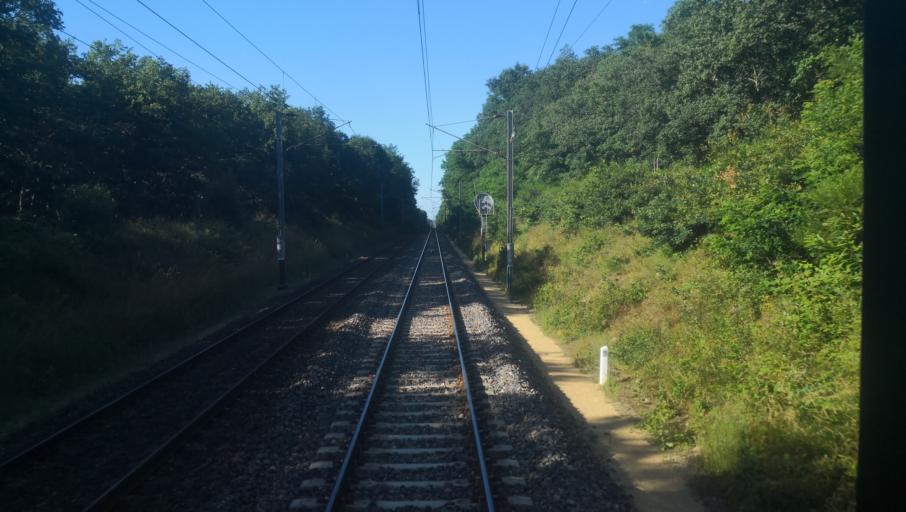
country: FR
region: Centre
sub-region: Departement du Cher
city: Saint-Satur
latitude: 47.3521
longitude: 2.8861
